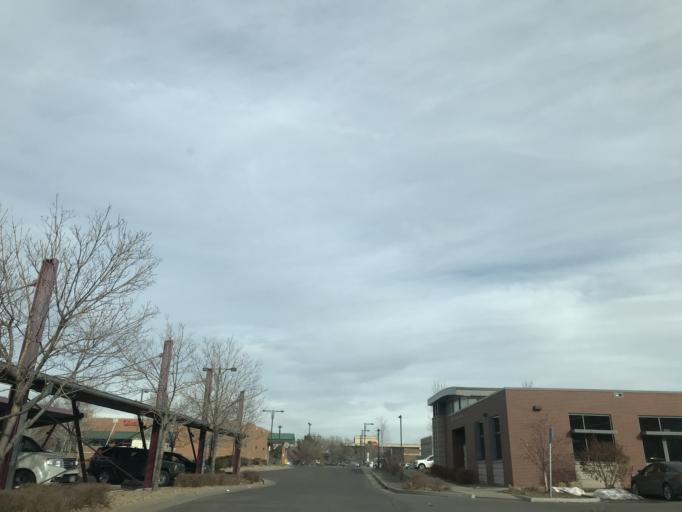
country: US
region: Colorado
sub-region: Adams County
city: Commerce City
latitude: 39.7587
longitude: -104.9017
